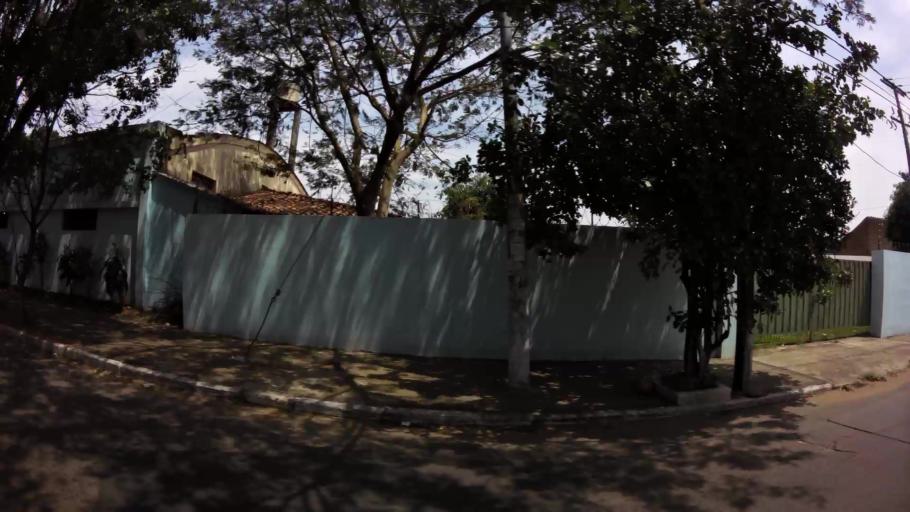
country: PY
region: Central
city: Lambare
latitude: -25.3198
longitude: -57.5997
